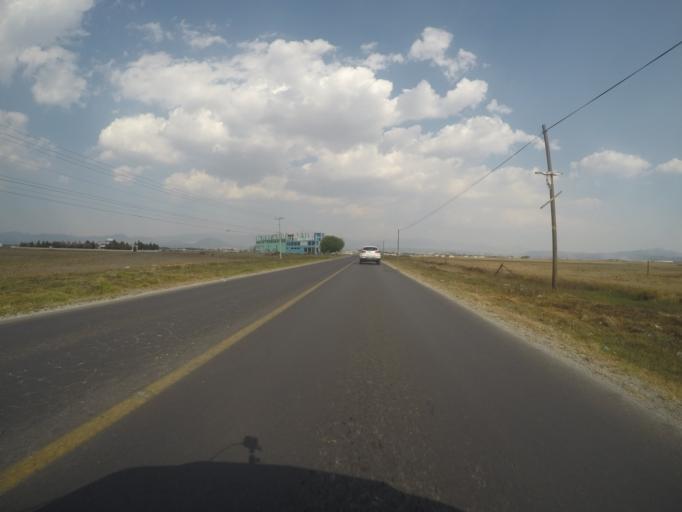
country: MX
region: Morelos
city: Chapultepec
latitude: 19.1916
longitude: -99.5343
